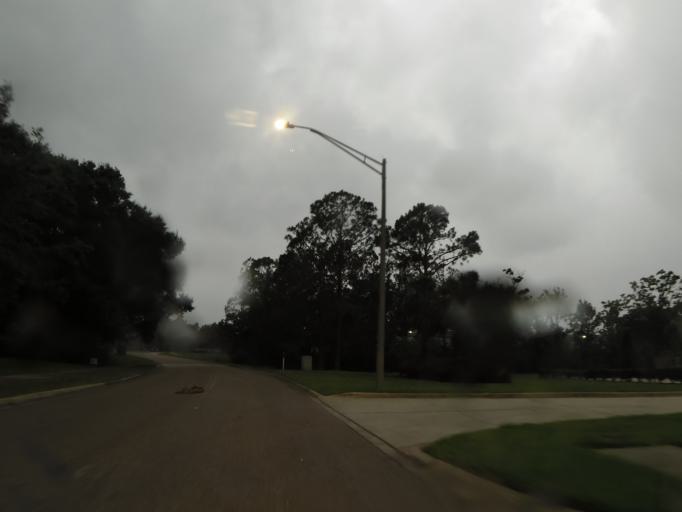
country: US
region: Florida
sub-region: Duval County
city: Neptune Beach
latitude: 30.2825
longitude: -81.5144
